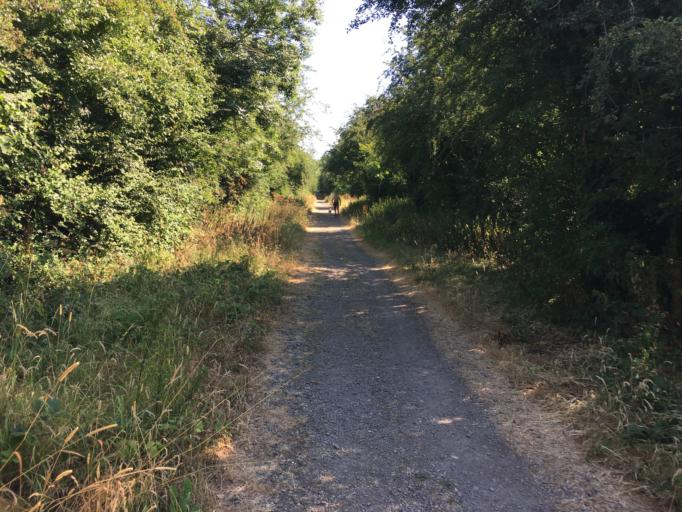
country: GB
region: England
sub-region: Warwickshire
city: Rugby
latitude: 52.3934
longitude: -1.2336
